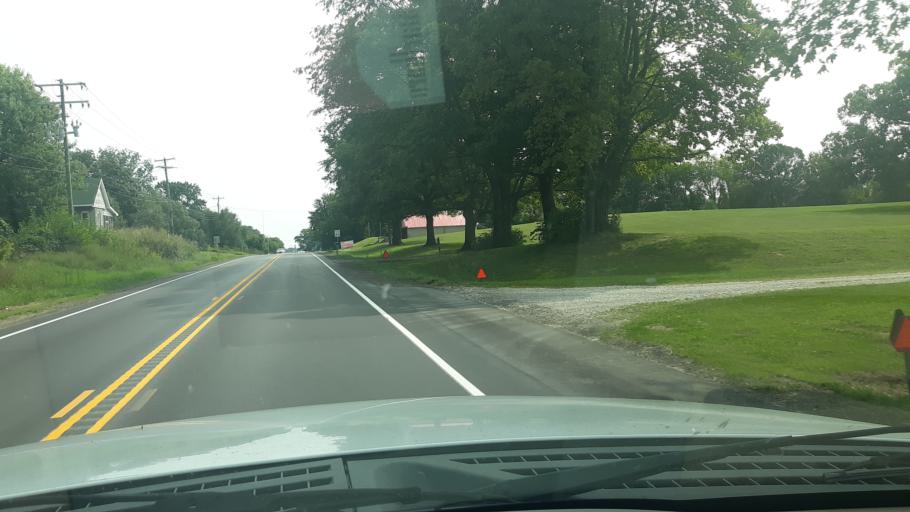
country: US
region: Indiana
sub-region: Gibson County
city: Princeton
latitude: 38.3556
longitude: -87.6186
